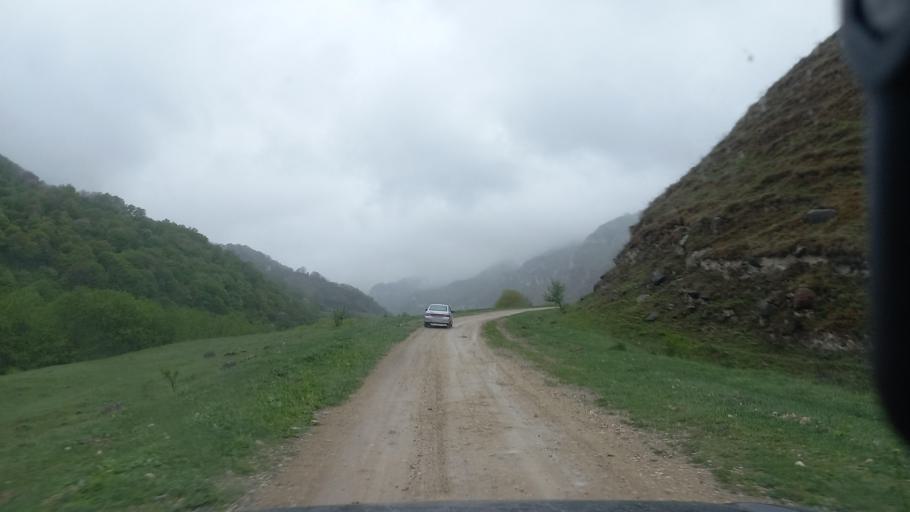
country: RU
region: Kabardino-Balkariya
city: Gundelen
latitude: 43.5967
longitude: 43.0671
